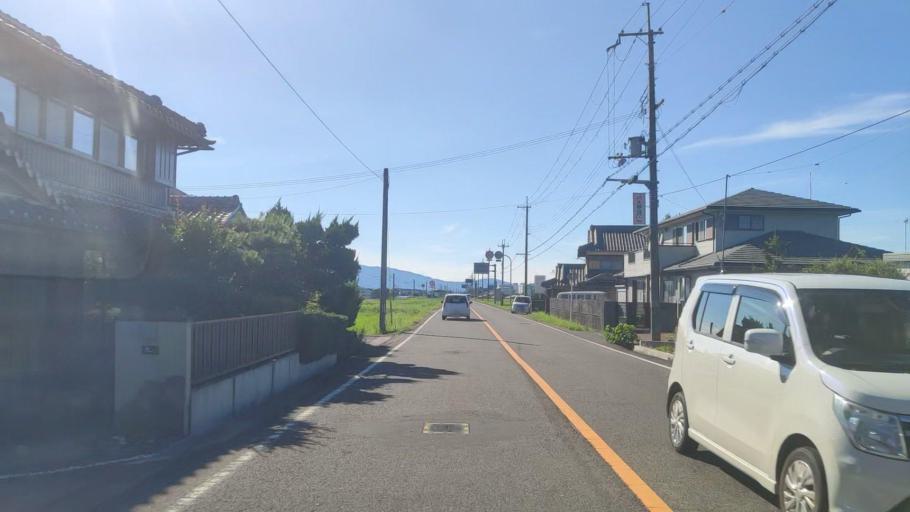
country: JP
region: Shiga Prefecture
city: Minakuchicho-matoba
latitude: 34.8932
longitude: 136.2254
